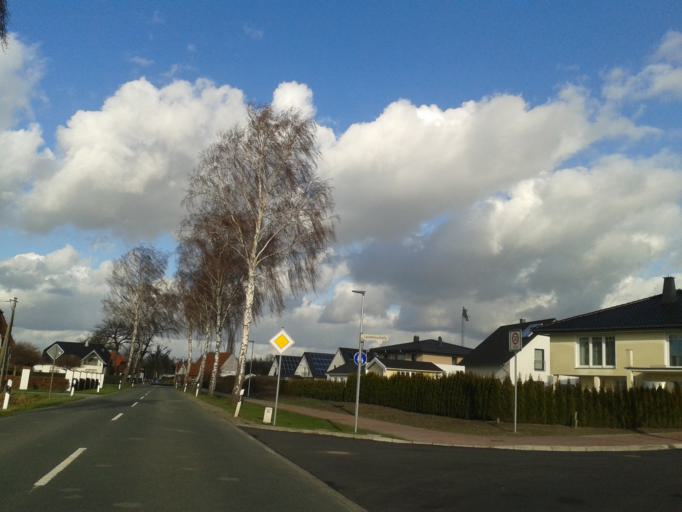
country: DE
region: North Rhine-Westphalia
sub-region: Regierungsbezirk Detmold
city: Salzkotten
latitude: 51.7031
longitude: 8.5802
